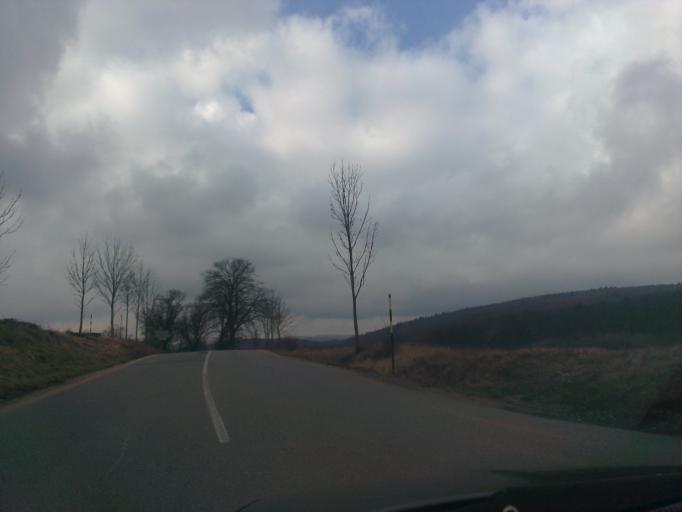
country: CZ
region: South Moravian
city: Bilovice nad Svitavou
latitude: 49.2618
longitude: 16.7295
